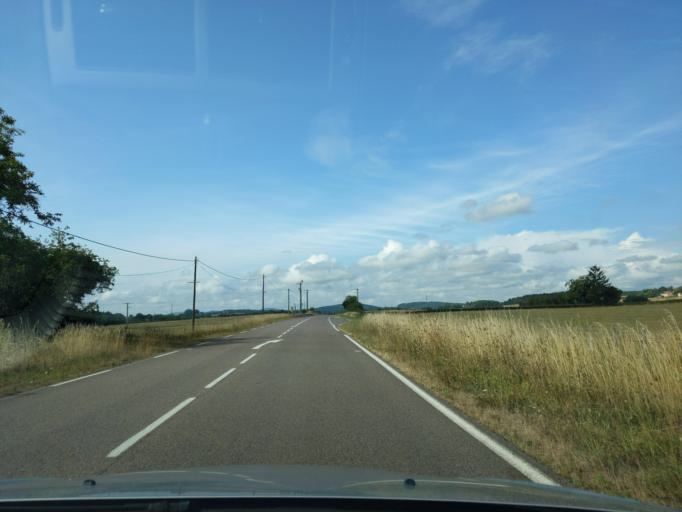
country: FR
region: Bourgogne
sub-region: Departement de Saone-et-Loire
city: Etang-sur-Arroux
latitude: 46.9131
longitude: 4.1729
